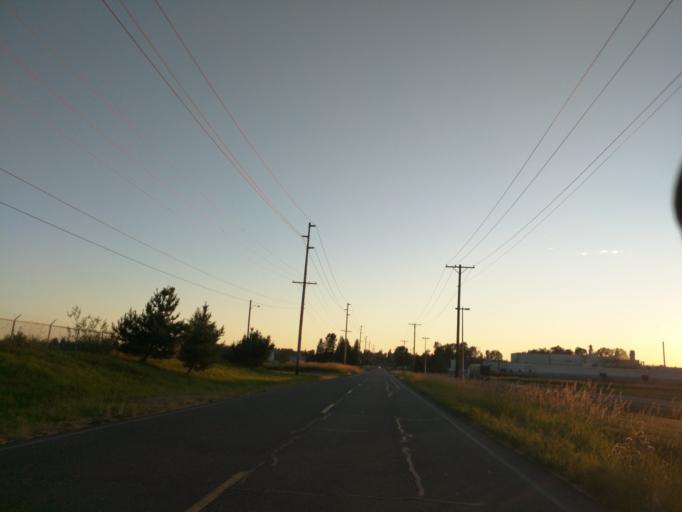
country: US
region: Washington
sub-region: Whatcom County
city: Sumas
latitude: 48.9927
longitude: -122.2749
